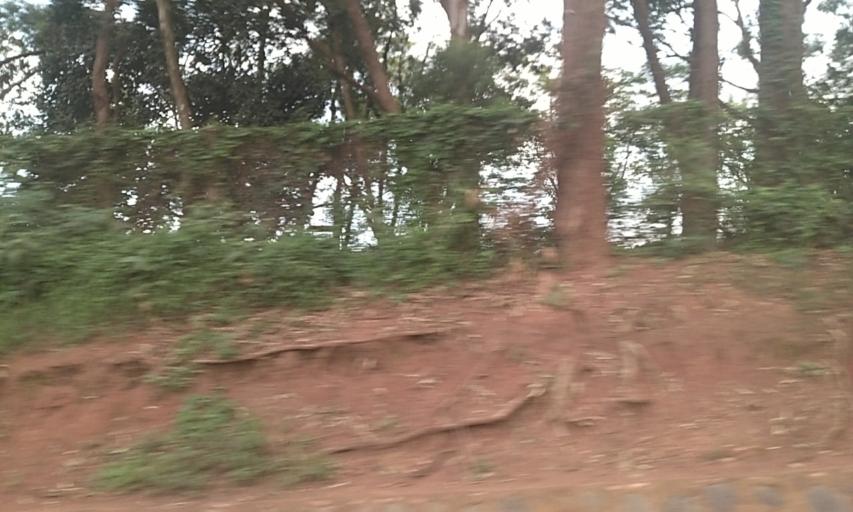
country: UG
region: Central Region
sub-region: Wakiso District
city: Kireka
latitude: 0.3448
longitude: 32.6254
